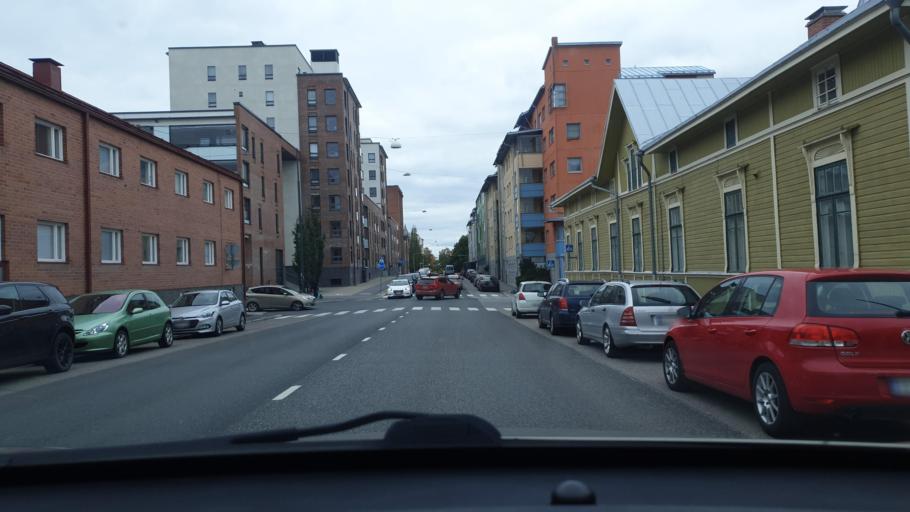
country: FI
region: Ostrobothnia
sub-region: Vaasa
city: Vaasa
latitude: 63.0942
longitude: 21.6238
